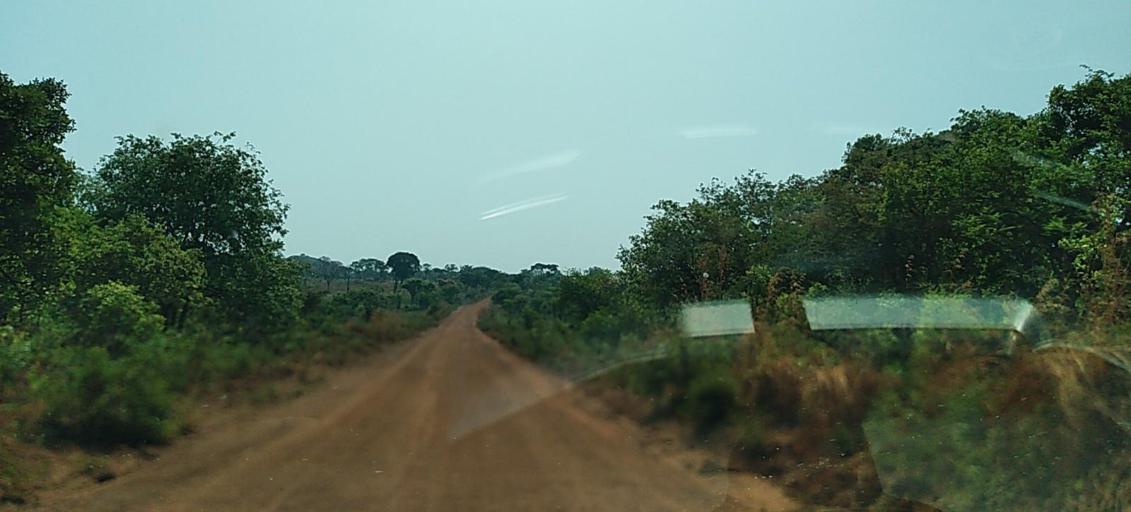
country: ZM
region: North-Western
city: Kansanshi
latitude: -12.0057
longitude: 26.5319
